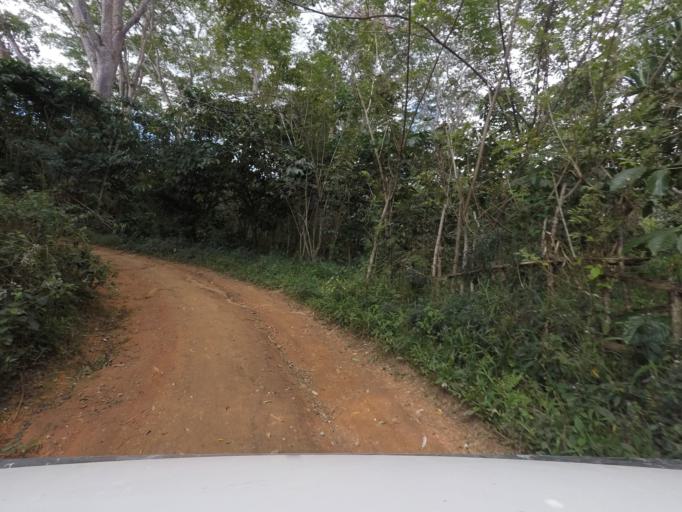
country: TL
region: Ermera
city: Gleno
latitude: -8.7194
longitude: 125.3194
